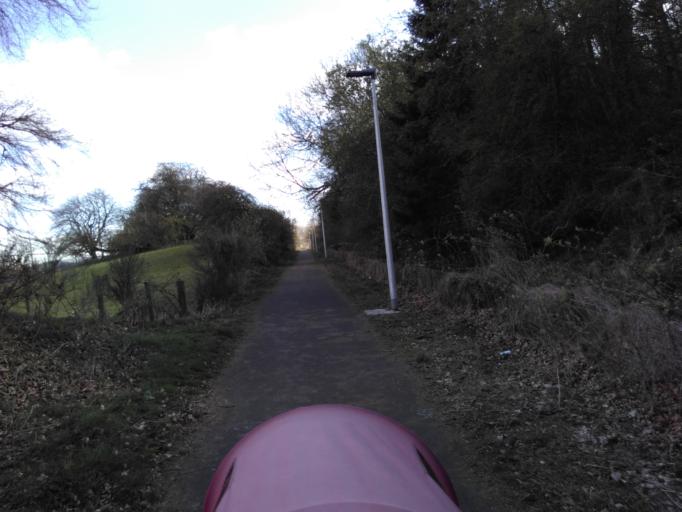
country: GB
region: Scotland
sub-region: Midlothian
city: Loanhead
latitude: 55.8836
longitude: -3.1453
